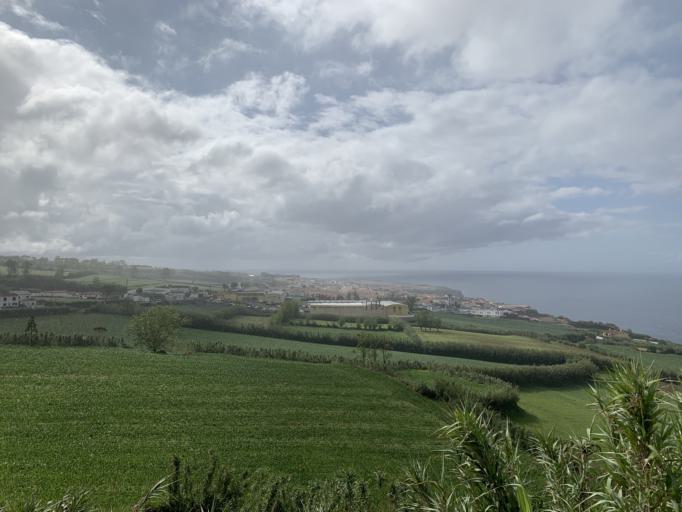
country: PT
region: Azores
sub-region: Ponta Delgada
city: Arrifes
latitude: 37.7589
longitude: -25.7272
